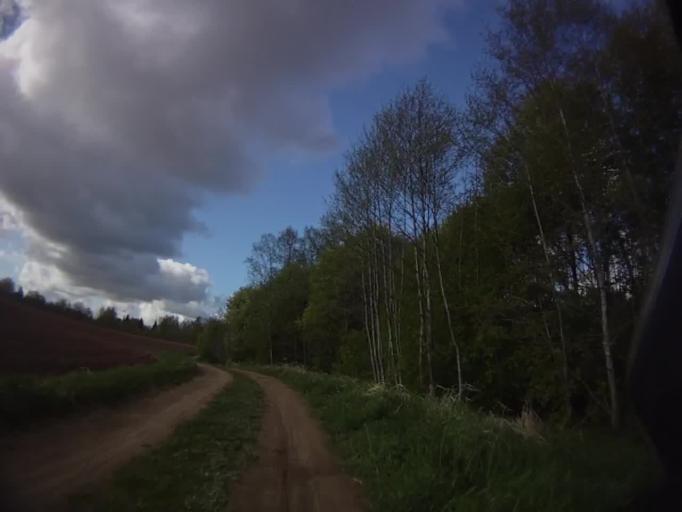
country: LV
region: Sigulda
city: Sigulda
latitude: 57.1659
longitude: 24.9069
